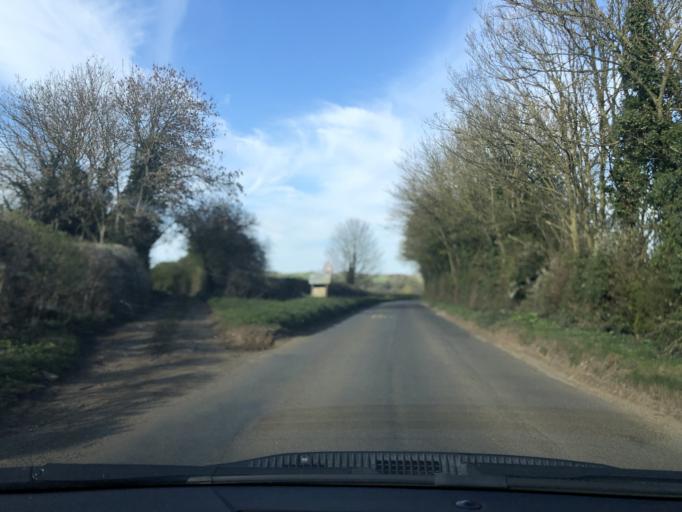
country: GB
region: England
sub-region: Oxfordshire
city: Bloxham
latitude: 52.0277
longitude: -1.4199
